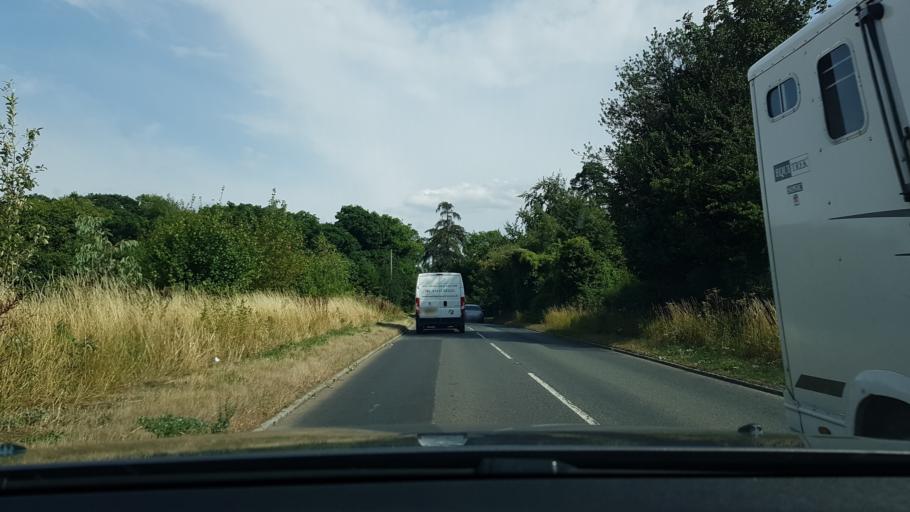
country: GB
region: England
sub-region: West Berkshire
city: Lambourn
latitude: 51.4701
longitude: -1.5114
